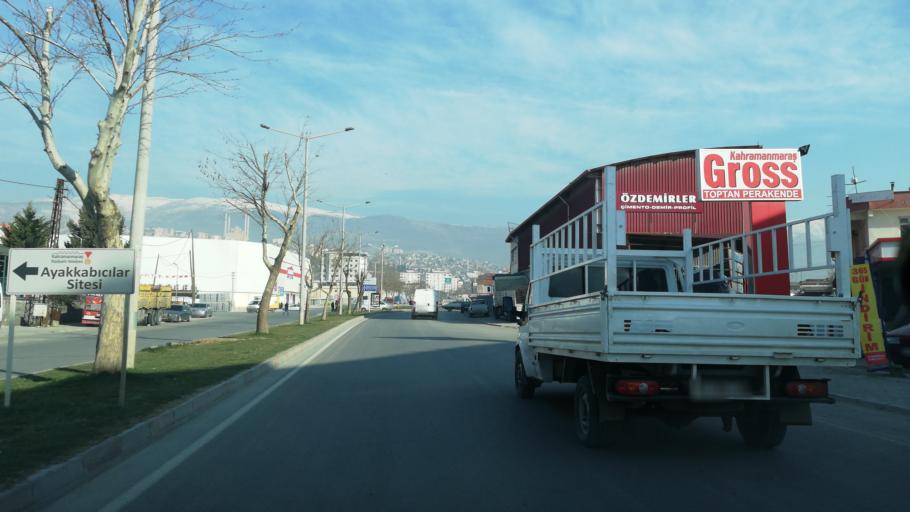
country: TR
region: Kahramanmaras
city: Kahramanmaras
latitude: 37.5644
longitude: 36.9171
